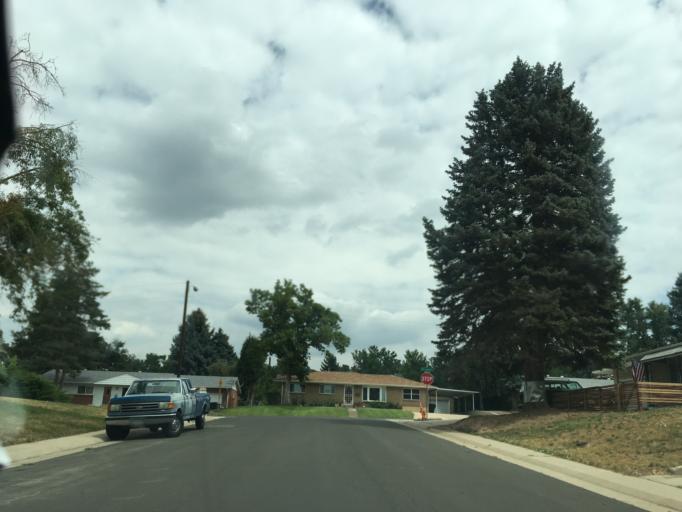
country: US
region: Colorado
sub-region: Arapahoe County
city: Sheridan
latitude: 39.6630
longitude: -105.0362
